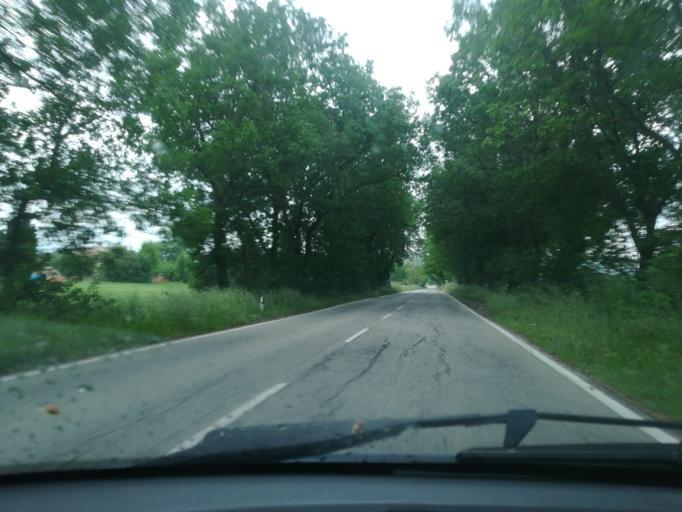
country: IT
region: The Marches
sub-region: Provincia di Macerata
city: Pollenza
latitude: 43.2892
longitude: 13.3809
